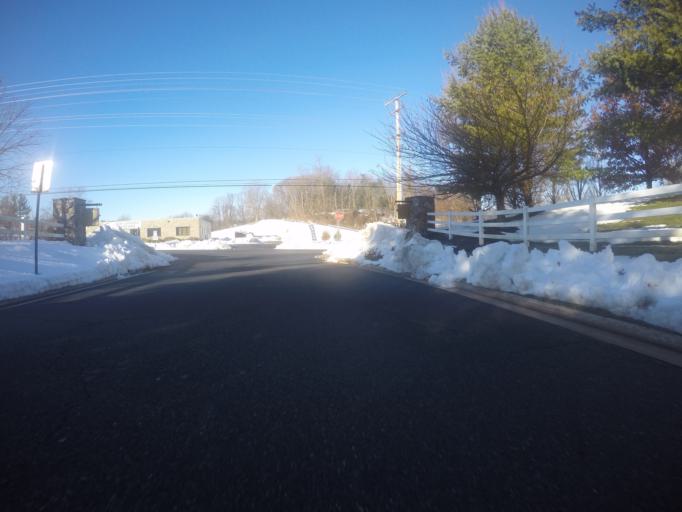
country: US
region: Maryland
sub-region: Baltimore County
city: Hunt Valley
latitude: 39.5301
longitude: -76.6450
